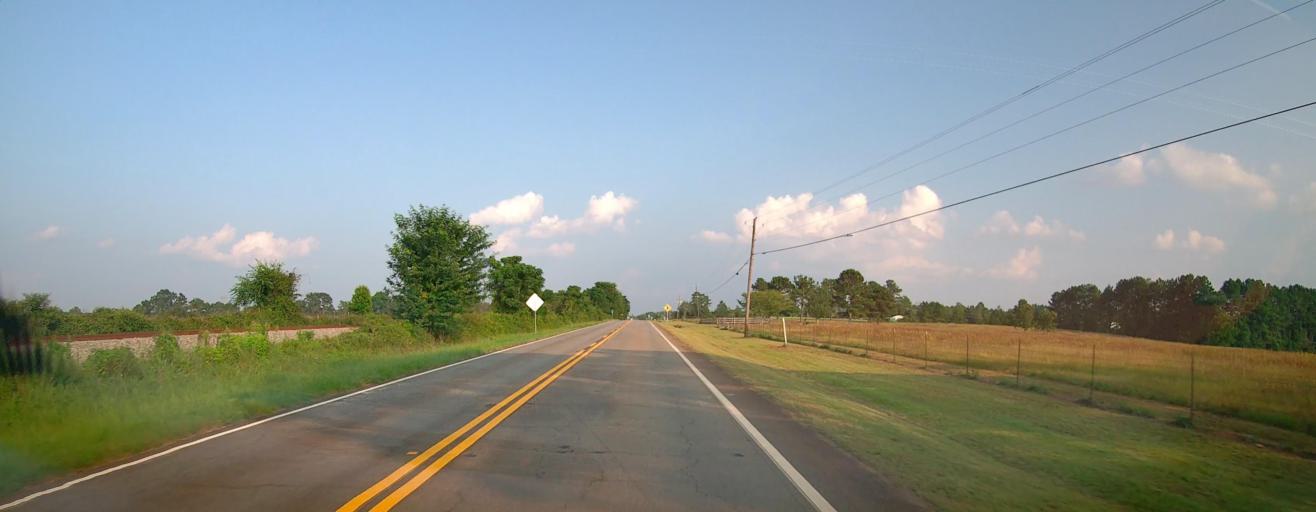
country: US
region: Georgia
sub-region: Jones County
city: Gray
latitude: 33.0378
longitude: -83.5444
